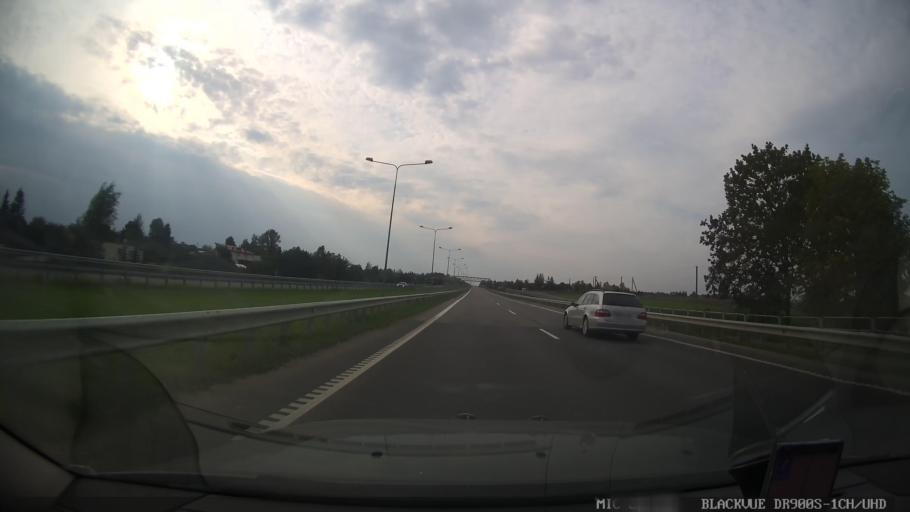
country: LT
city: Skaidiskes
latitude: 54.6400
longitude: 25.3634
